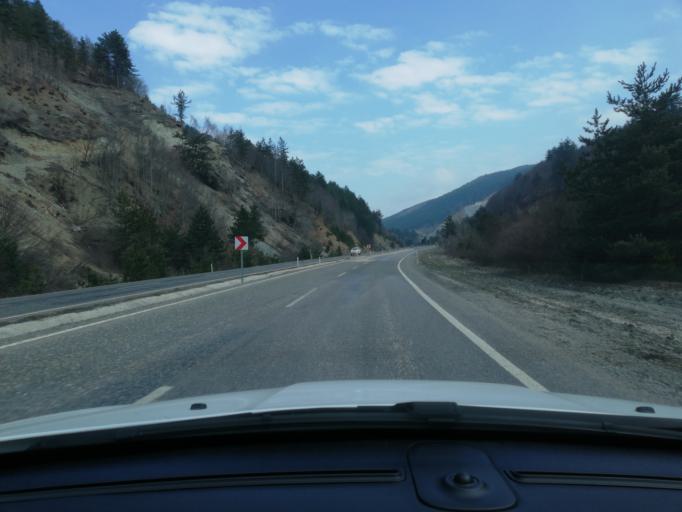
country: TR
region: Kastamonu
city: Kuzyaka
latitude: 41.1695
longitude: 33.7938
